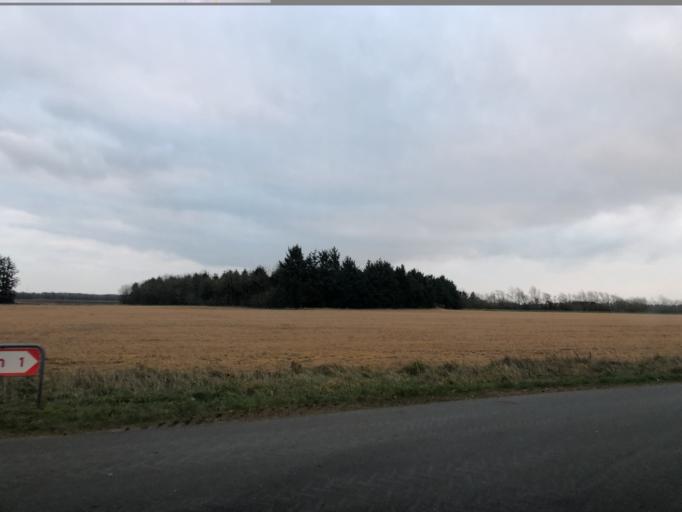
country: DK
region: Central Jutland
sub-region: Holstebro Kommune
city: Ulfborg
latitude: 56.2432
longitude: 8.2896
